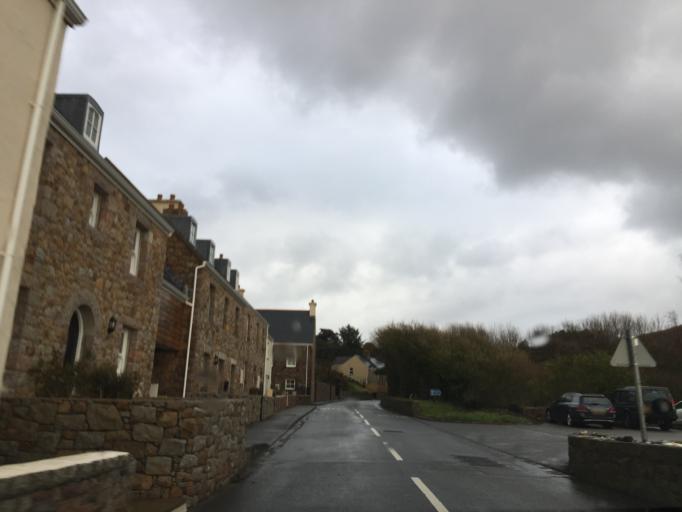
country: JE
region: St Helier
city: Saint Helier
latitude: 49.2355
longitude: -2.2296
